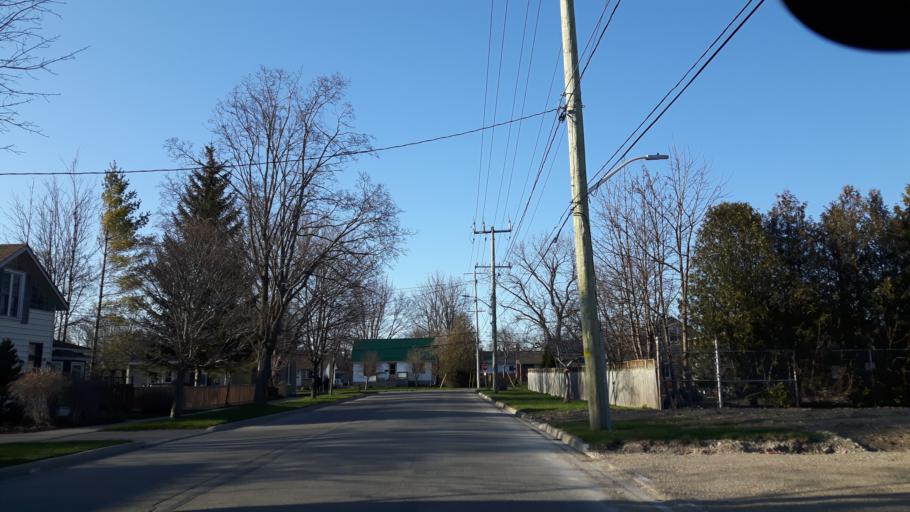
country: CA
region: Ontario
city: Goderich
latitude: 43.7384
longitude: -81.7164
